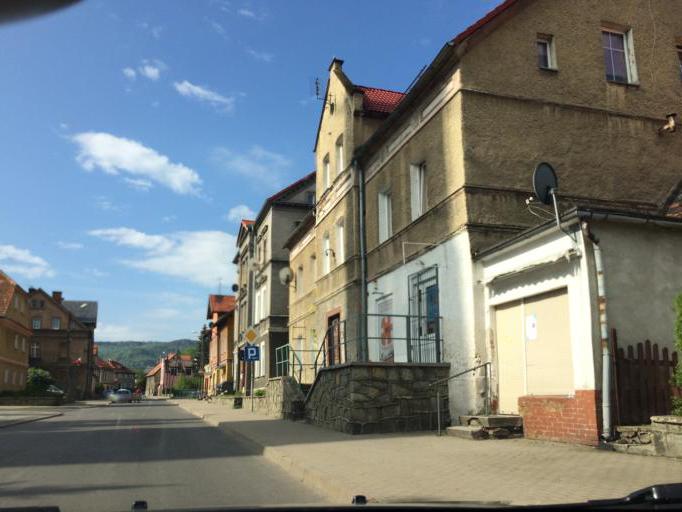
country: PL
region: Lower Silesian Voivodeship
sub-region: Powiat dzierzoniowski
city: Pieszyce
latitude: 50.7114
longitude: 16.5802
